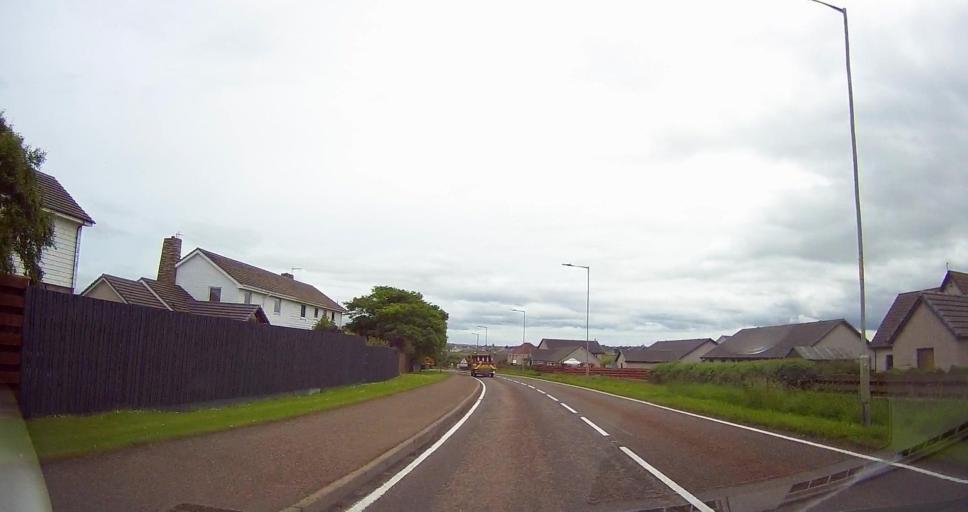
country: GB
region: Scotland
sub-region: Highland
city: Thurso
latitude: 58.6030
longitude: -3.5485
